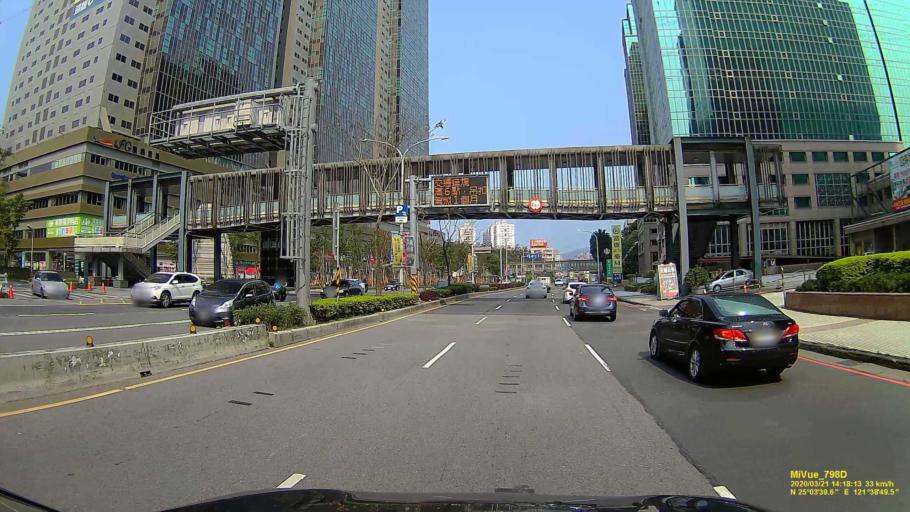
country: TW
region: Taipei
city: Taipei
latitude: 25.0617
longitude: 121.6468
